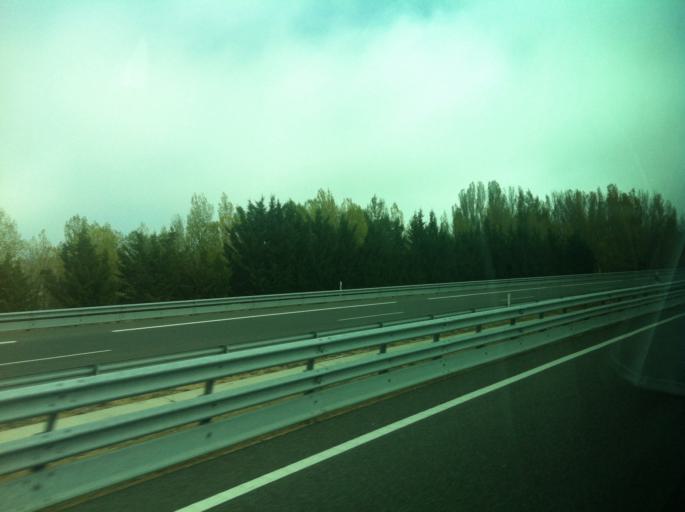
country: ES
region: Castille and Leon
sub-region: Provincia de Burgos
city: Quintana del Pidio
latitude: 41.7611
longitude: -3.6892
